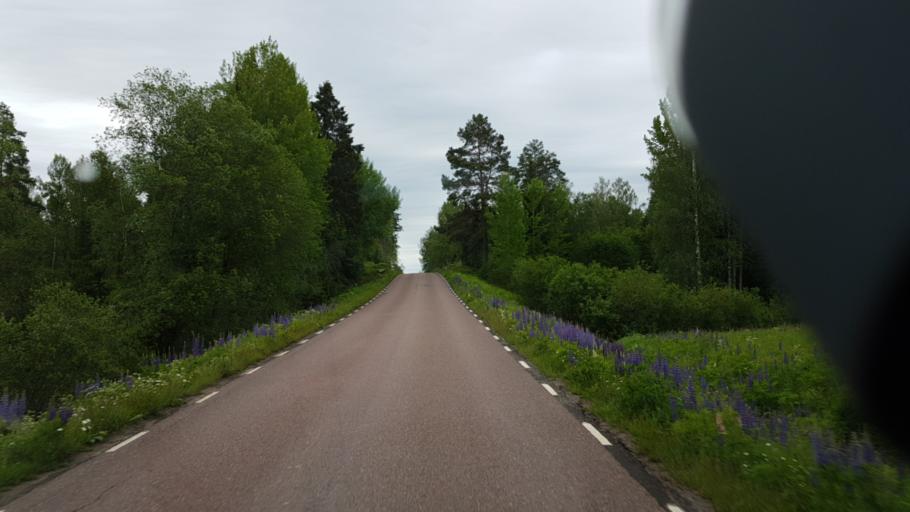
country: NO
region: Ostfold
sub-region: Romskog
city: Romskog
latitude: 59.7411
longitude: 12.0568
